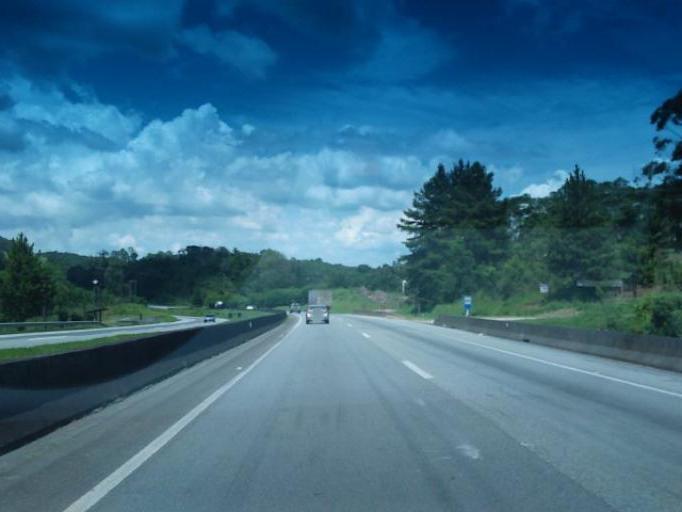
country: BR
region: Sao Paulo
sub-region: Juquitiba
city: Juquitiba
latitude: -23.9661
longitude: -47.1300
